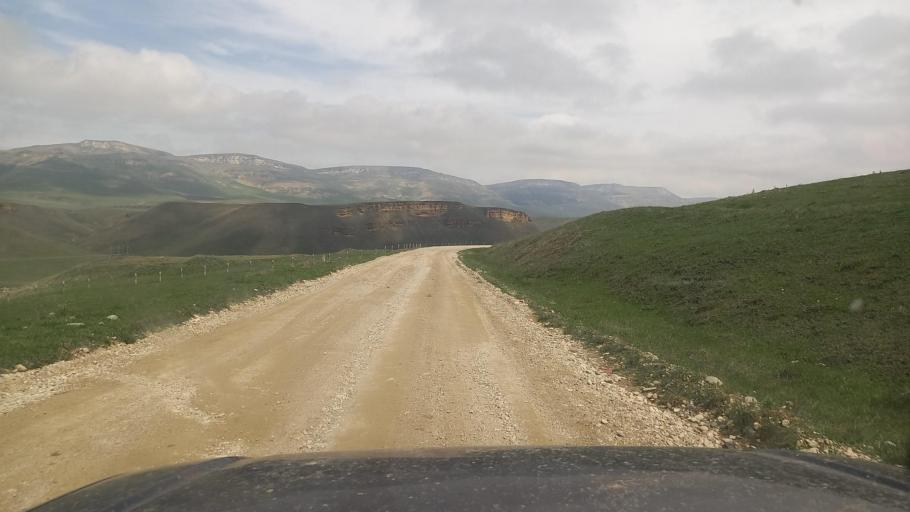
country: RU
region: Stavropol'skiy
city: Kislovodsk
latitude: 43.7989
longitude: 42.8710
